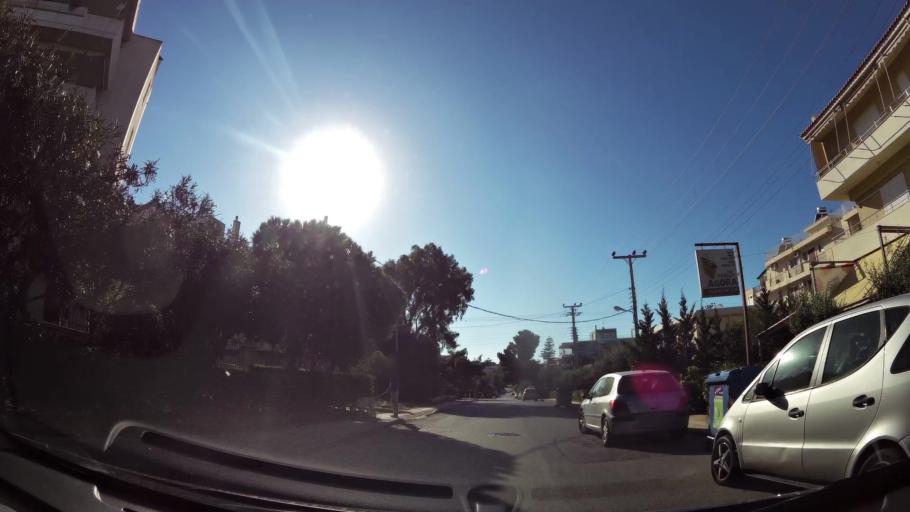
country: GR
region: Attica
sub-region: Nomarchia Athinas
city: Glyfada
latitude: 37.8615
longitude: 23.7662
